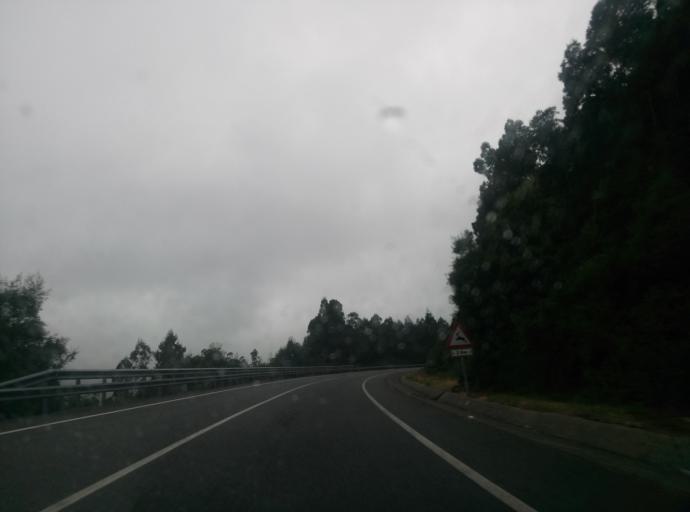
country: ES
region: Galicia
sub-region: Provincia de Lugo
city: Viveiro
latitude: 43.5612
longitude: -7.6433
